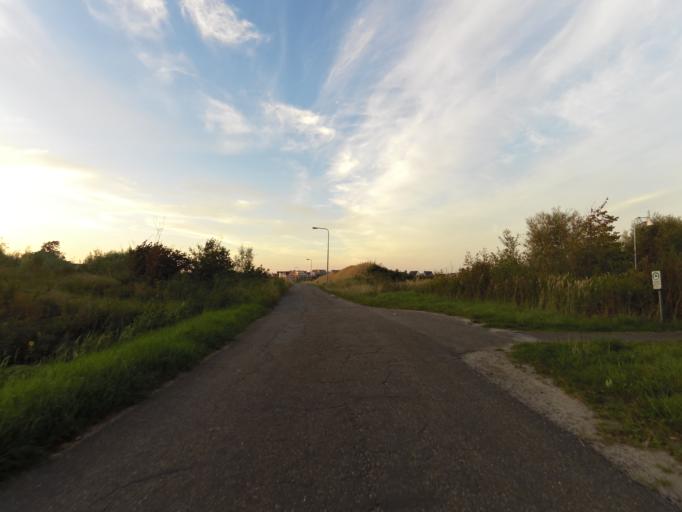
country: NL
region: South Holland
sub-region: Gemeente Katwijk
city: Rijnsburg
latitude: 52.1732
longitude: 4.4503
